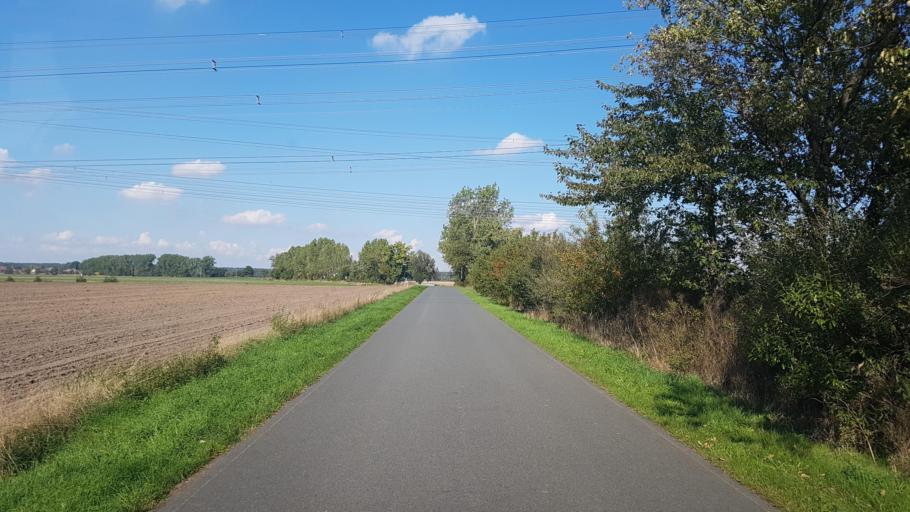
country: DE
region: Brandenburg
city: Ihlow
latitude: 51.8365
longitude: 13.2835
